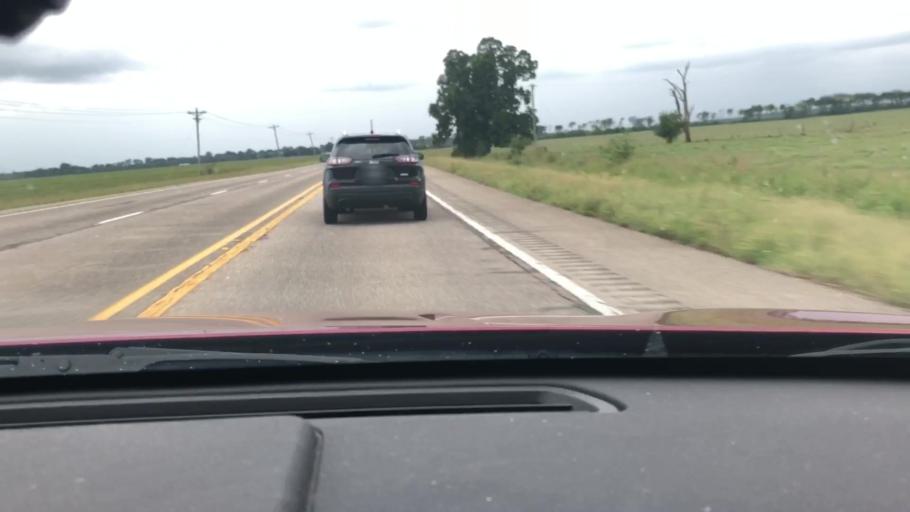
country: US
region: Arkansas
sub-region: Lafayette County
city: Lewisville
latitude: 33.3887
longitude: -93.7360
